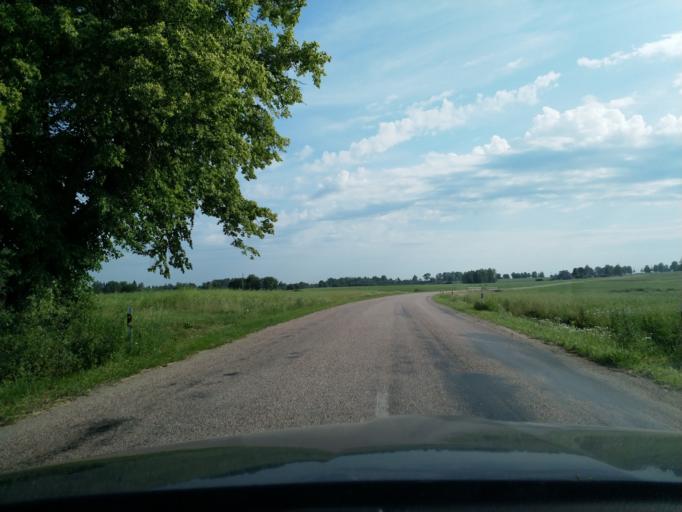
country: LV
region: Talsu Rajons
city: Sabile
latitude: 56.9304
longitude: 22.5669
